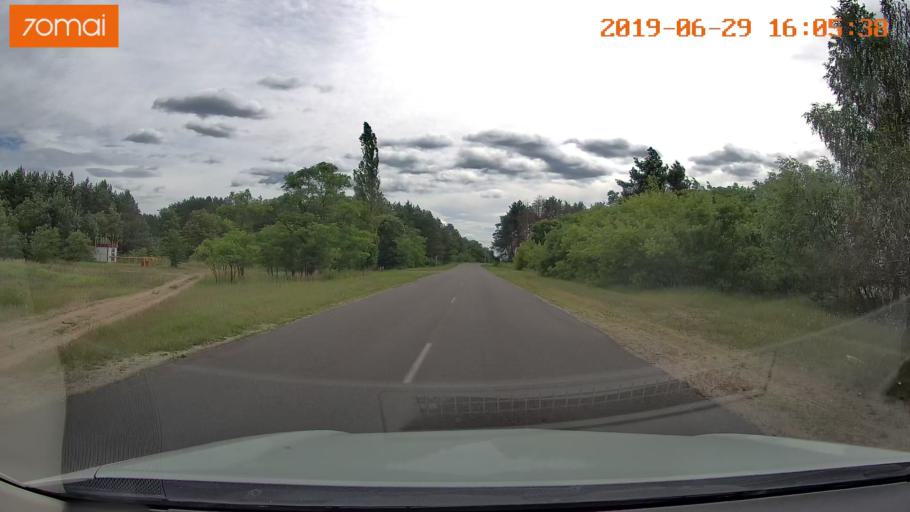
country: BY
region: Brest
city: Luninyets
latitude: 52.2152
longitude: 27.0184
